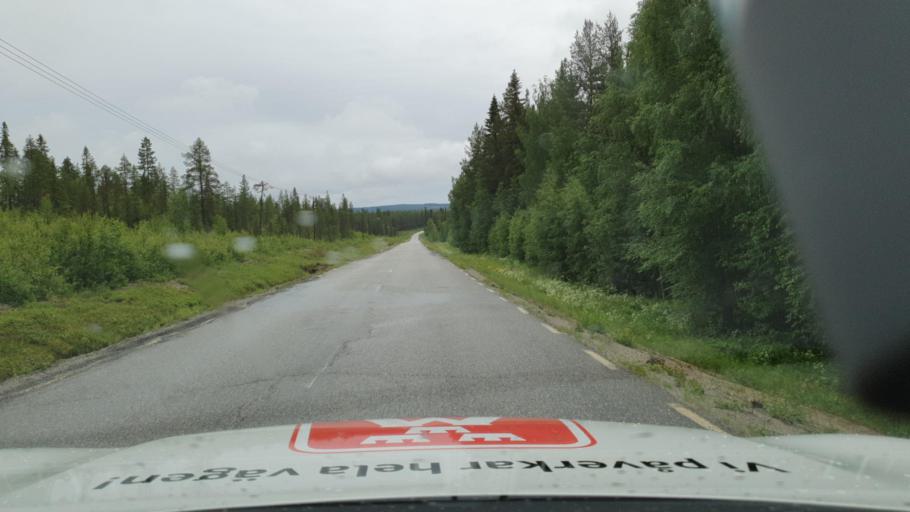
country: SE
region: Vaesterbotten
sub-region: Asele Kommun
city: Asele
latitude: 63.9946
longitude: 17.1707
